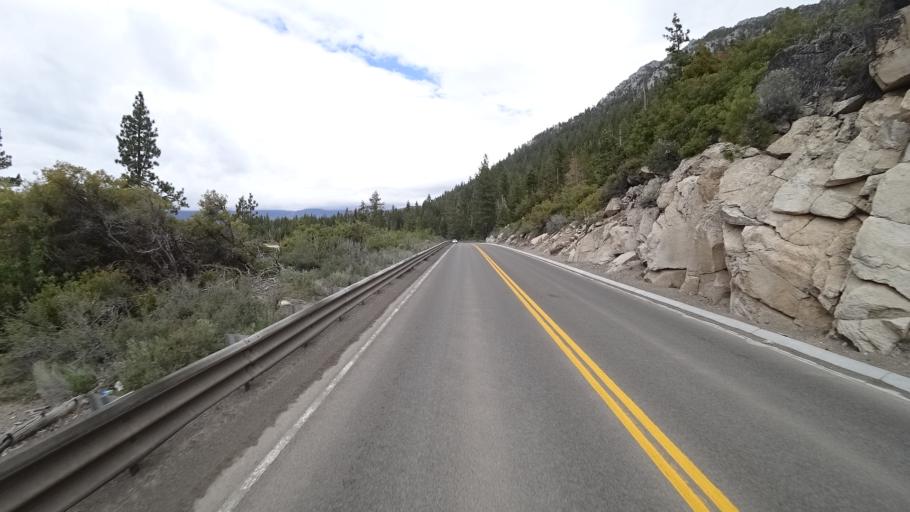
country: US
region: Nevada
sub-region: Washoe County
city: Incline Village
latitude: 39.1925
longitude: -119.9269
